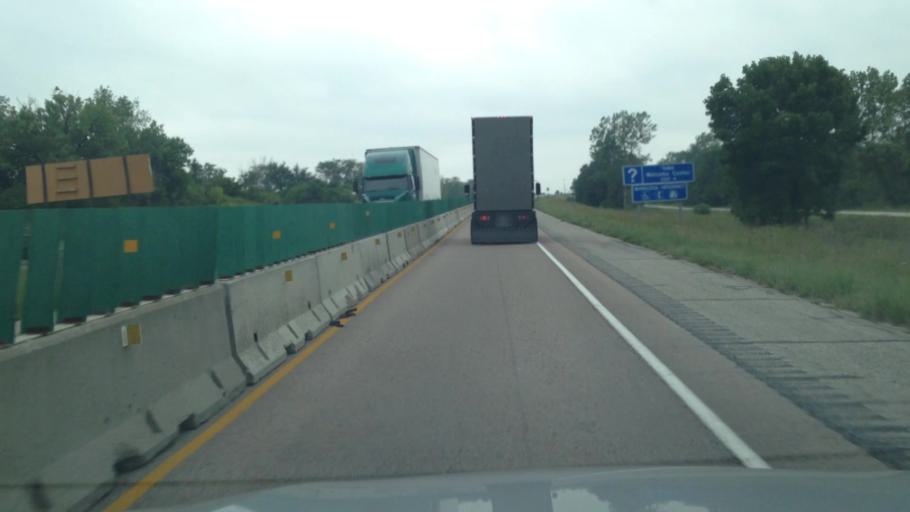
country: US
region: Iowa
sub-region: Decatur County
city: Lamoni
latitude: 40.6465
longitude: -93.8661
